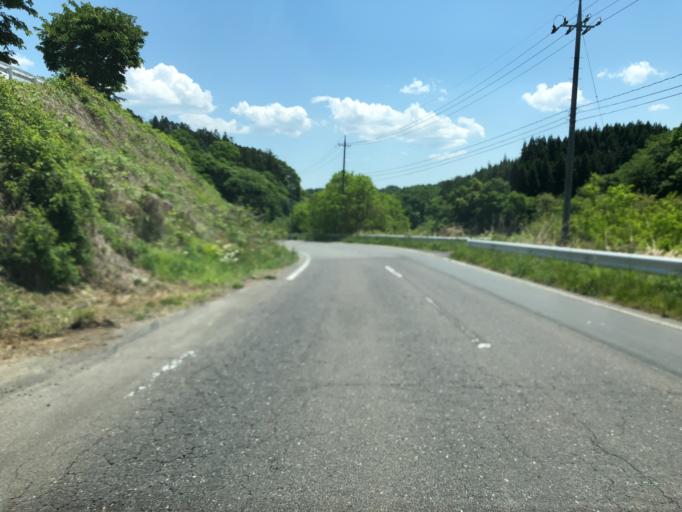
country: JP
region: Fukushima
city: Funehikimachi-funehiki
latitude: 37.4824
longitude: 140.5636
